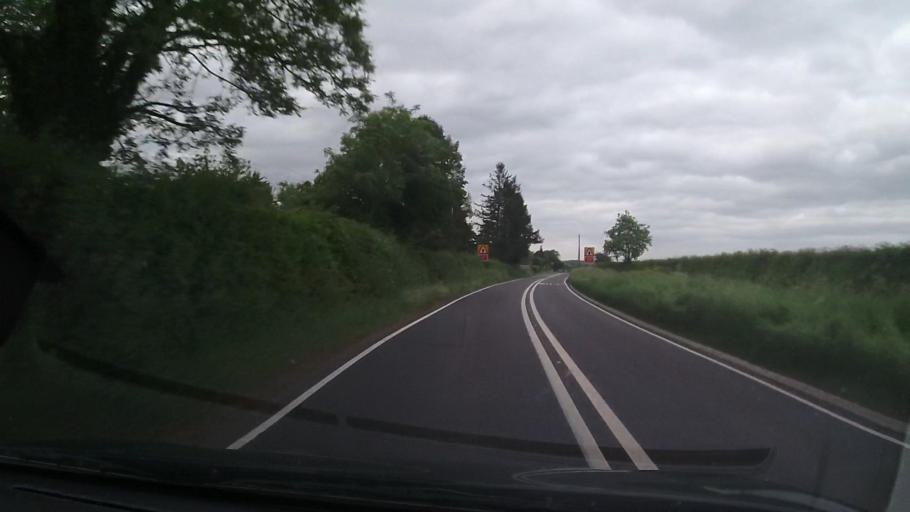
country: GB
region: England
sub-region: Shropshire
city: Clive
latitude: 52.8081
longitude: -2.7503
